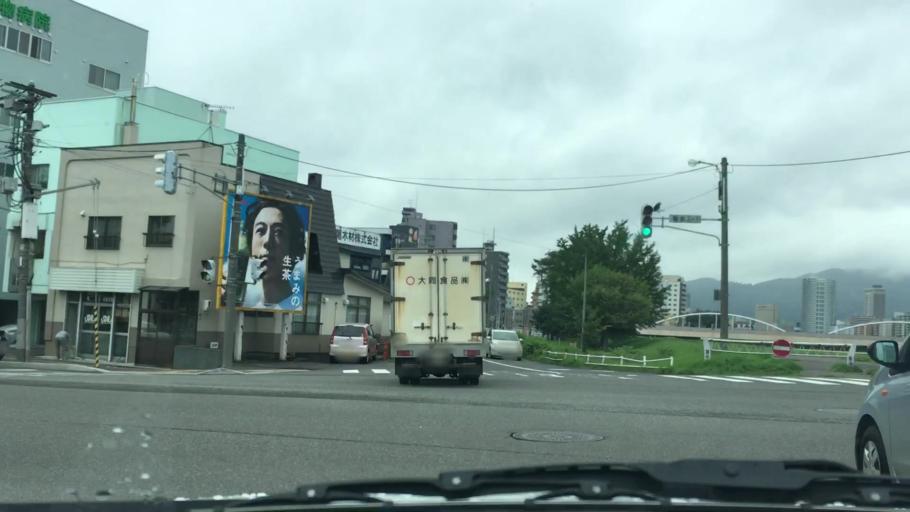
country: JP
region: Hokkaido
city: Sapporo
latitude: 43.0600
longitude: 141.3694
